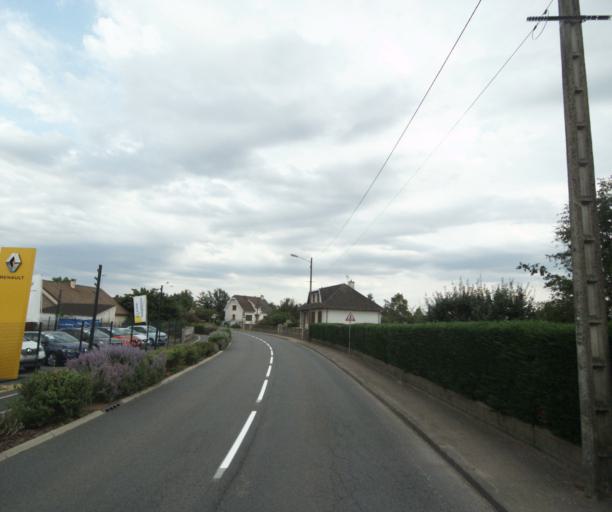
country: FR
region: Bourgogne
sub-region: Departement de Saone-et-Loire
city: Gueugnon
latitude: 46.5964
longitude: 4.0516
